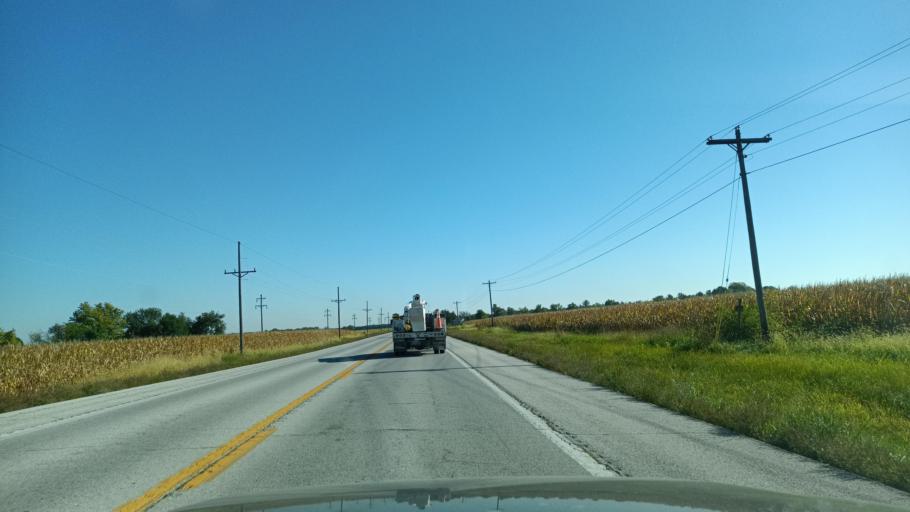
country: US
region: Missouri
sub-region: Audrain County
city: Vandalia
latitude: 39.4462
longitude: -91.6336
